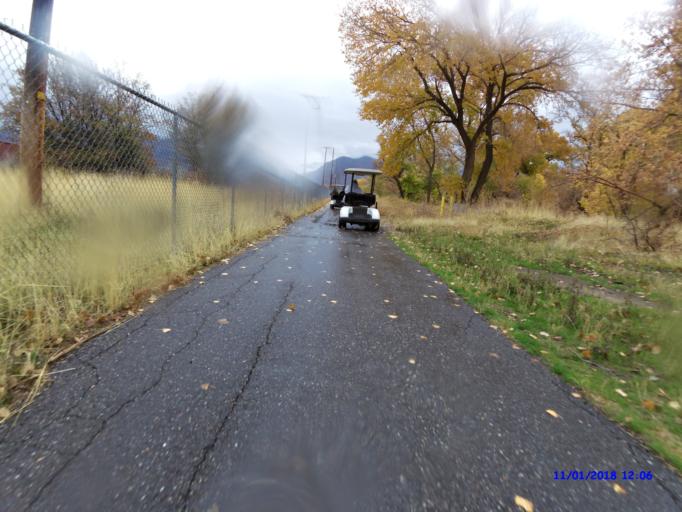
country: US
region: Utah
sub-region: Weber County
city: Ogden
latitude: 41.2294
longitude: -111.9921
